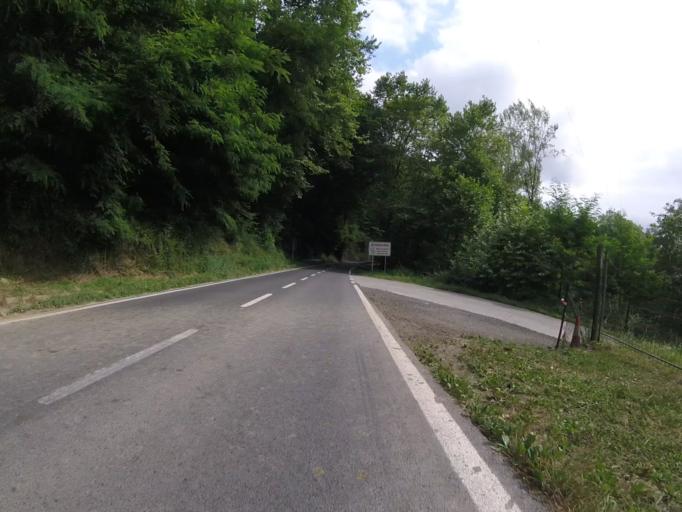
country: ES
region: Navarre
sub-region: Provincia de Navarra
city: Ituren
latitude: 43.1323
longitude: -1.7262
